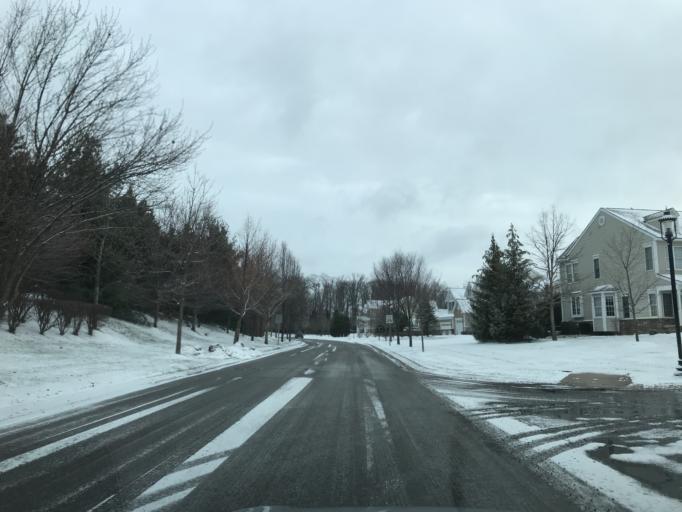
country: US
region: Michigan
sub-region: Oakland County
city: Wixom
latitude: 42.4840
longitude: -83.5444
